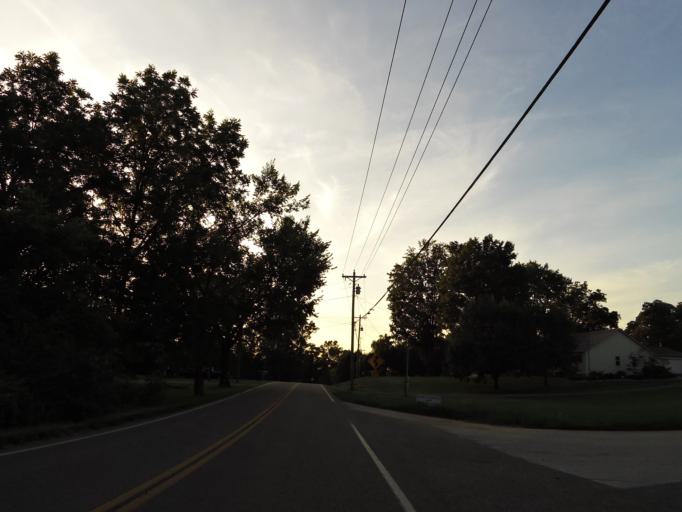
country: US
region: Tennessee
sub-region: Blount County
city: Maryville
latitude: 35.7029
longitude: -83.9660
